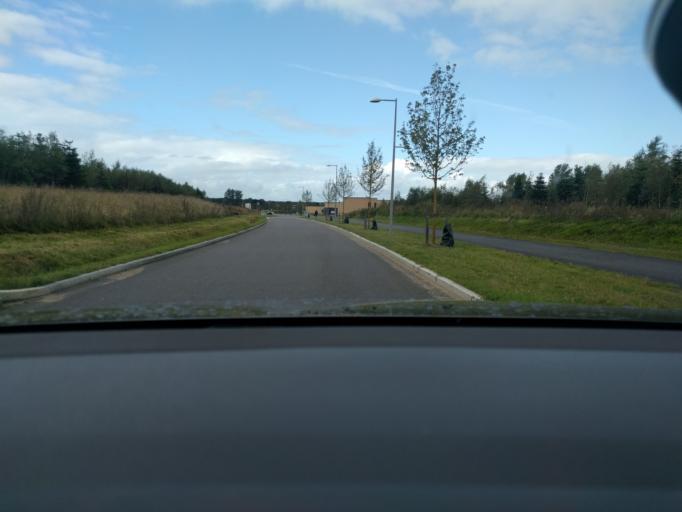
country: DK
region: Central Jutland
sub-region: Viborg Kommune
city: Viborg
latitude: 56.4244
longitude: 9.4171
